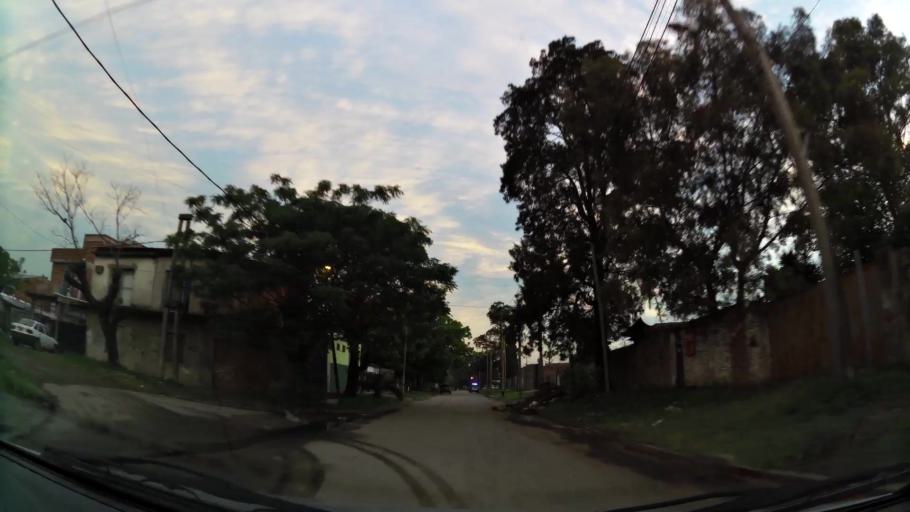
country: AR
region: Buenos Aires
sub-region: Partido de Lomas de Zamora
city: Lomas de Zamora
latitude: -34.7546
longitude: -58.3652
